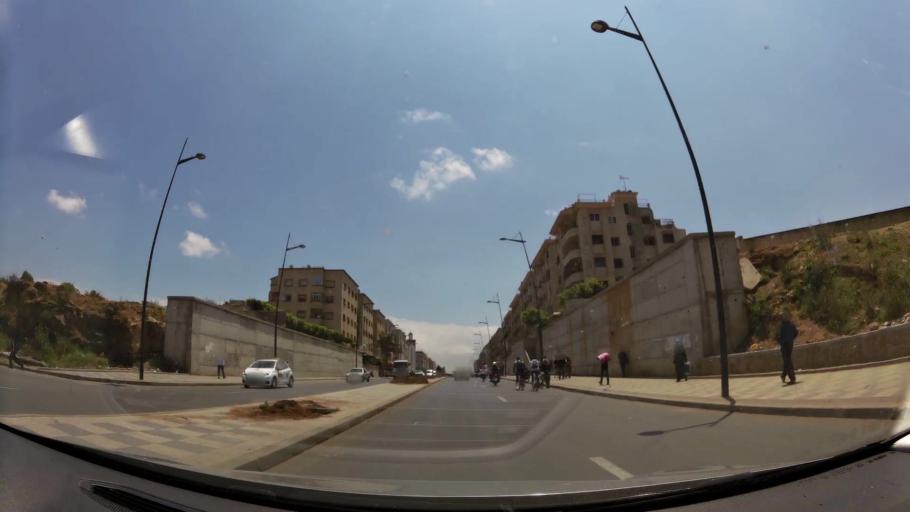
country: MA
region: Rabat-Sale-Zemmour-Zaer
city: Sale
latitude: 34.0650
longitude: -6.7864
